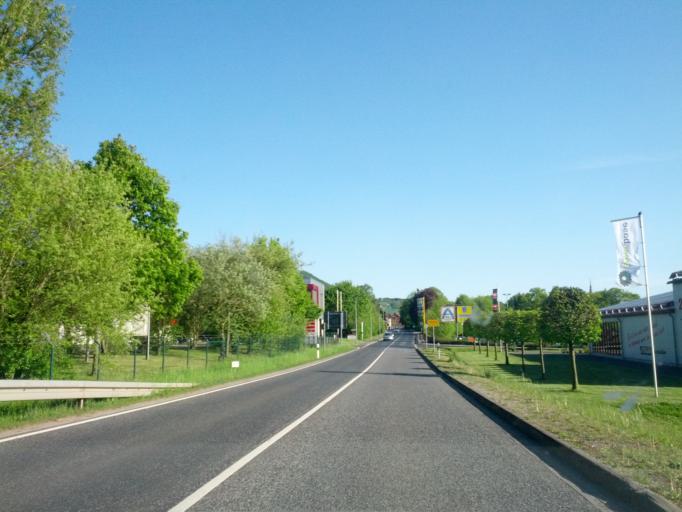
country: DE
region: Hesse
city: Wanfried
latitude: 51.1886
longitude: 10.1674
